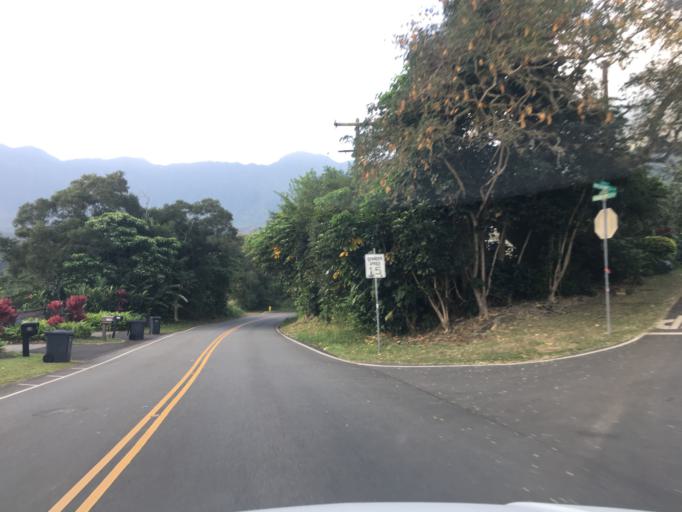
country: US
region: Hawaii
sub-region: Honolulu County
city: Maunawili
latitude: 21.3663
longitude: -157.7668
